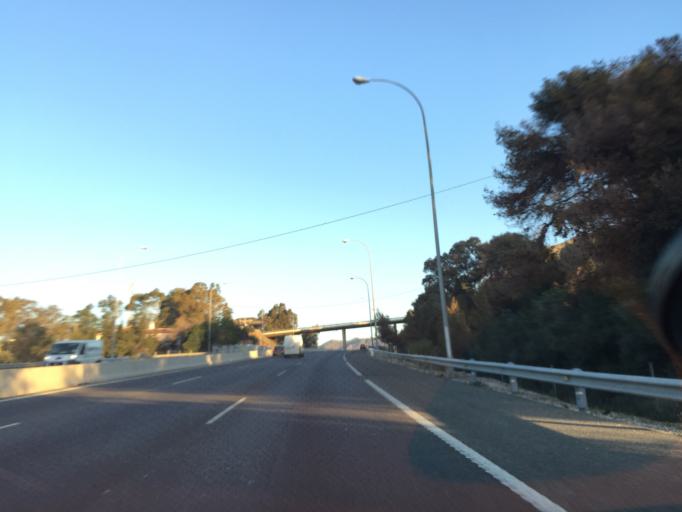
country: ES
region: Andalusia
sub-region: Provincia de Malaga
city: Malaga
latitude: 36.7444
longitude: -4.4067
